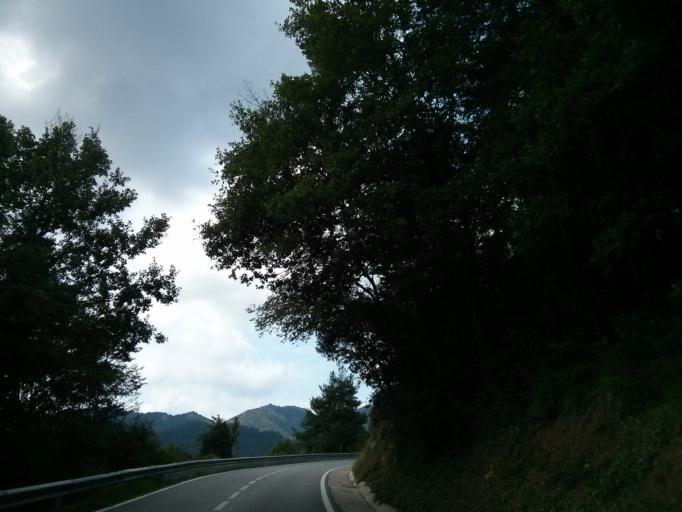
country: ES
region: Catalonia
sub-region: Provincia de Barcelona
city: Borreda
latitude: 42.1367
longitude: 1.9992
